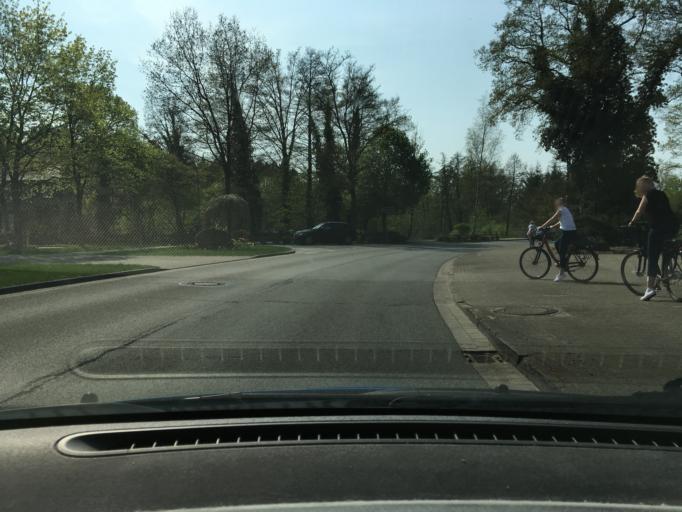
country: DE
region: Lower Saxony
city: Fassberg
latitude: 52.8757
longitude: 10.1209
